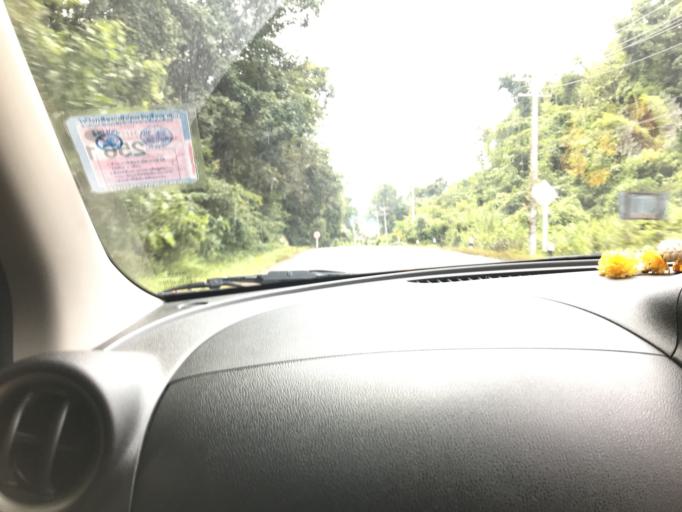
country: TH
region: Kanchanaburi
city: Sangkhla Buri
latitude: 15.1332
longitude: 98.5072
